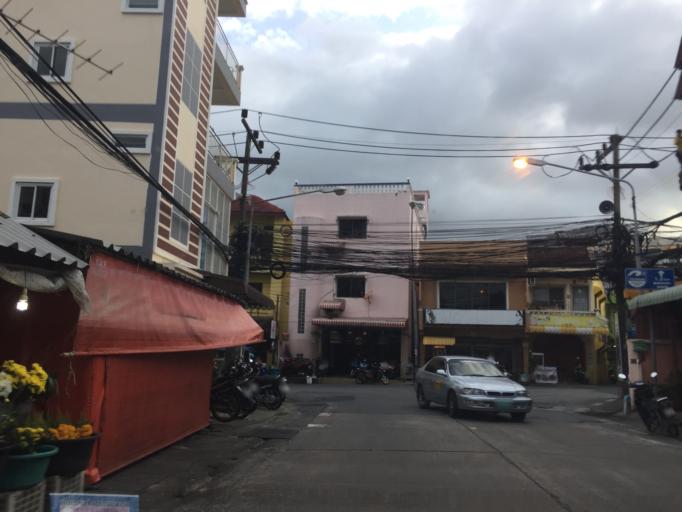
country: TH
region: Phuket
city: Patong
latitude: 7.8952
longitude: 98.3053
